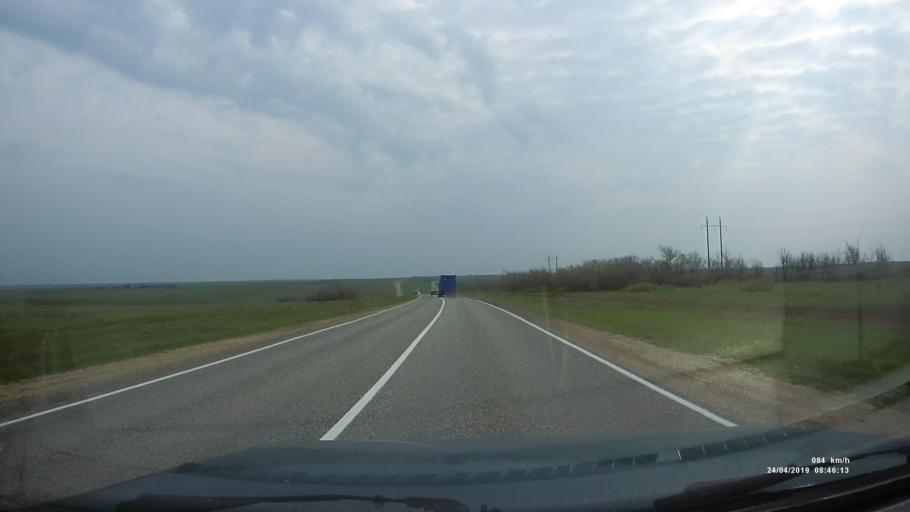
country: RU
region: Kalmykiya
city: Arshan'
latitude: 46.2375
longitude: 44.0752
